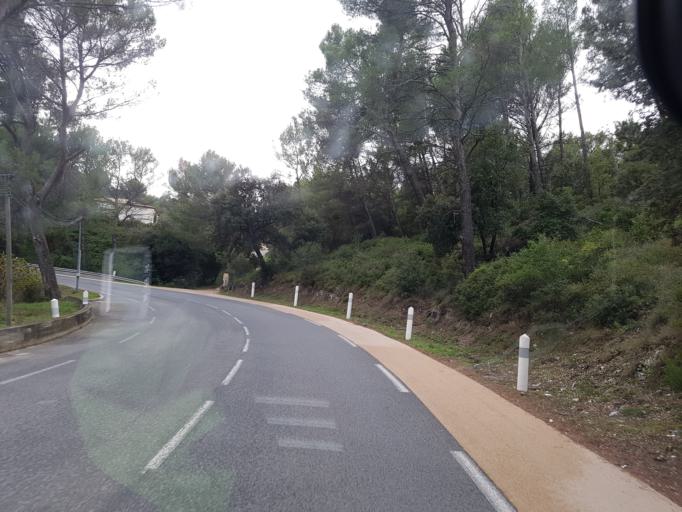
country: FR
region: Provence-Alpes-Cote d'Azur
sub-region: Departement des Bouches-du-Rhone
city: Cuges-les-Pins
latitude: 43.2674
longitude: 5.7378
